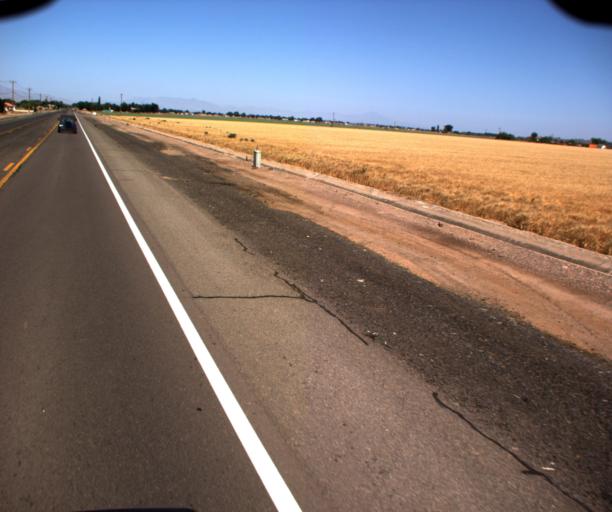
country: US
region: Arizona
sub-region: Graham County
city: Safford
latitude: 32.8167
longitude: -109.6613
